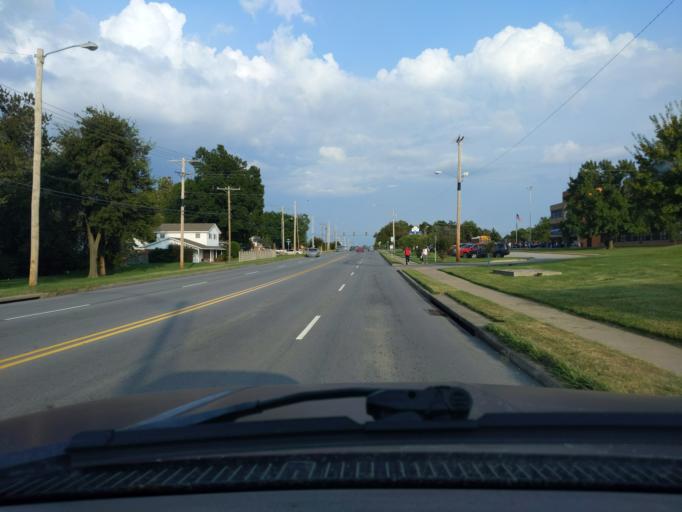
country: US
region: Oklahoma
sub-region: Tulsa County
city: Tulsa
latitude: 36.1334
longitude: -95.8986
